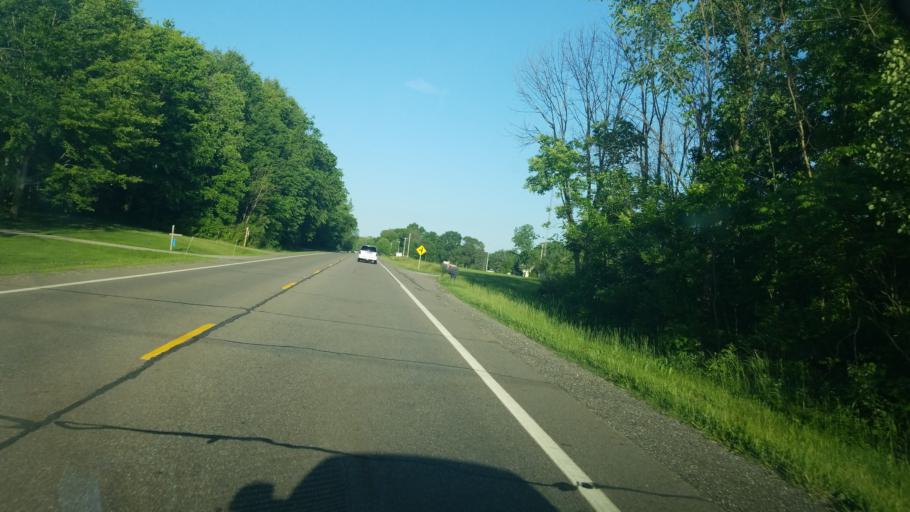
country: US
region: Ohio
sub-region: Portage County
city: Ravenna
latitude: 41.1534
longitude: -81.1910
